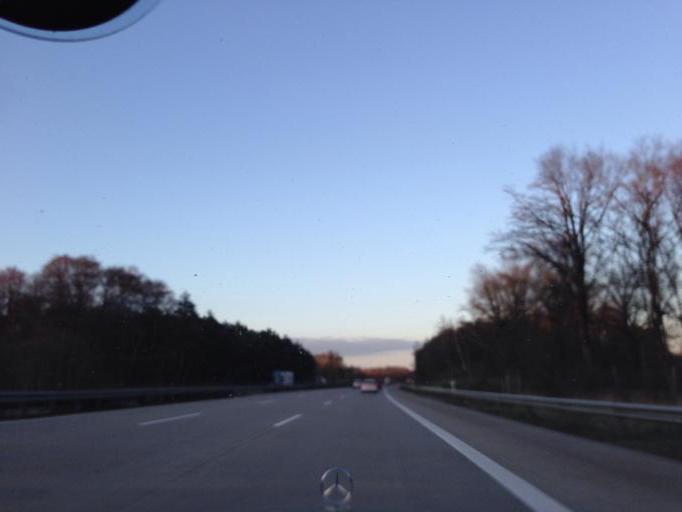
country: DE
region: Lower Saxony
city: Bispingen
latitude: 53.1437
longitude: 10.0109
